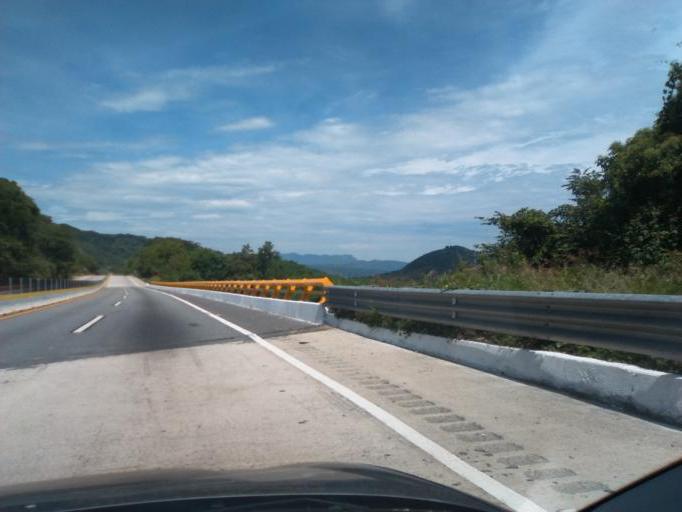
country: MX
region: Guerrero
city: Xaltianguis
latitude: 17.0132
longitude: -99.6599
